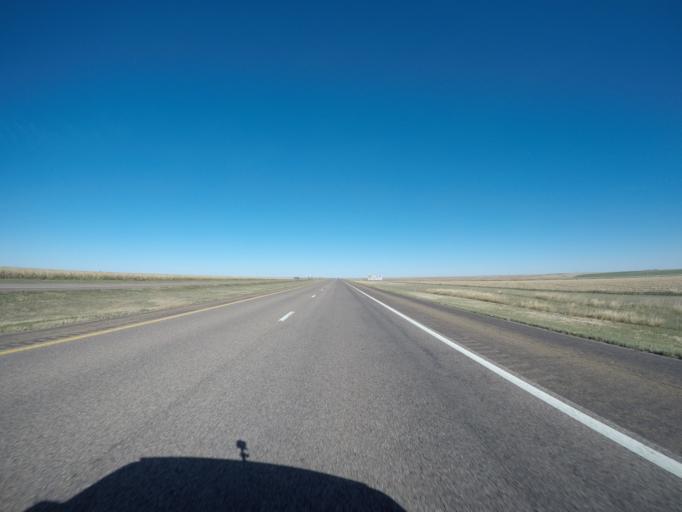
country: US
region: Kansas
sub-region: Thomas County
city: Colby
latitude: 39.3552
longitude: -101.3389
